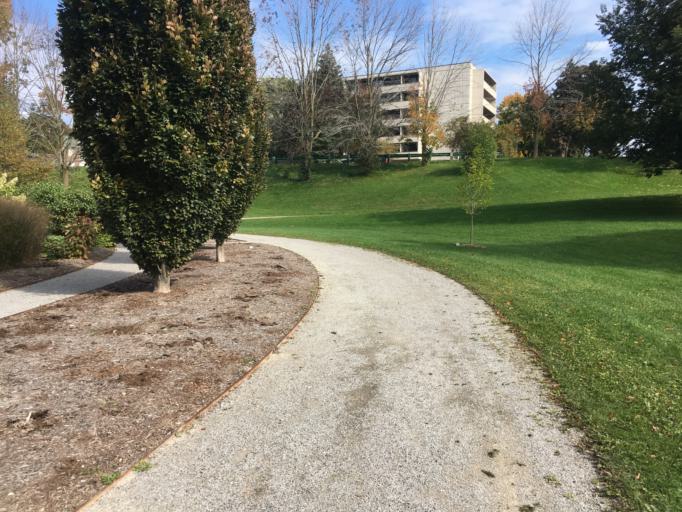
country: CA
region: Ontario
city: Oshawa
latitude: 43.9013
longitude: -78.8717
